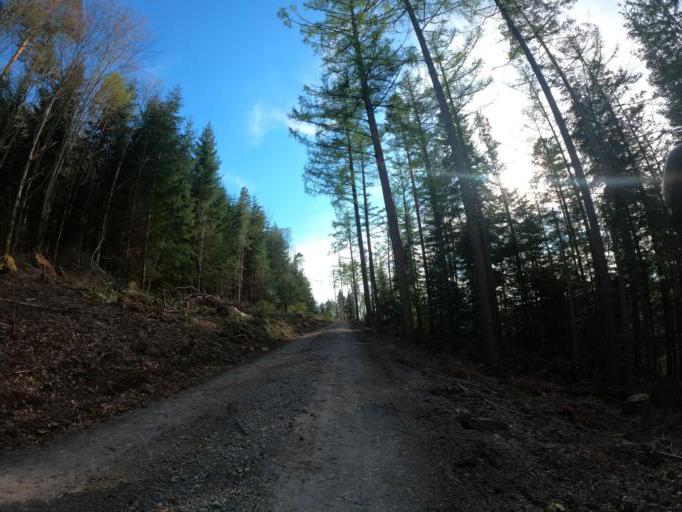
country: DE
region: Baden-Wuerttemberg
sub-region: Karlsruhe Region
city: Bad Wildbad
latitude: 48.7112
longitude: 8.5694
